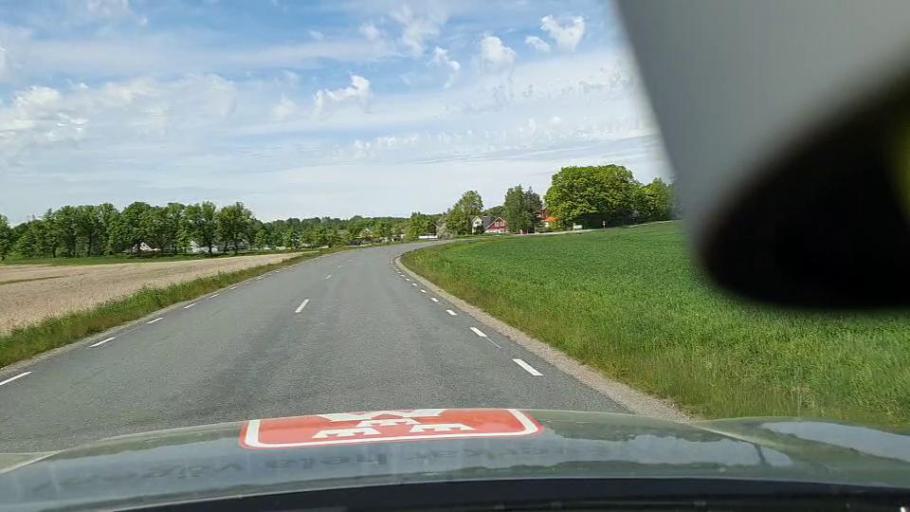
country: SE
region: Soedermanland
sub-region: Eskilstuna Kommun
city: Skogstorp
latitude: 59.3137
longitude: 16.4652
